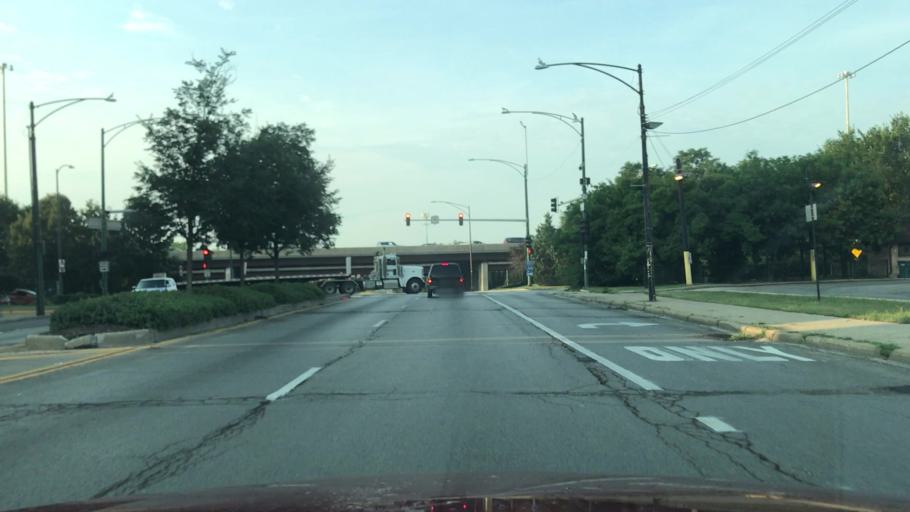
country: US
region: Illinois
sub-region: Cook County
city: Oak Park
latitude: 41.8724
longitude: -87.7646
